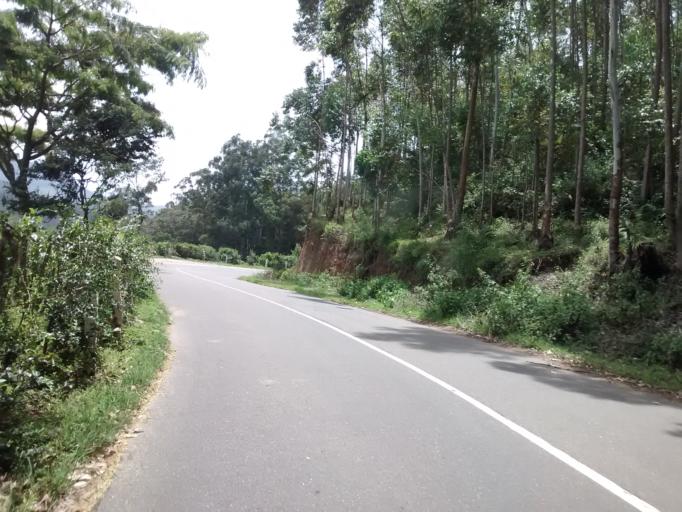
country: IN
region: Kerala
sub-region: Idukki
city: Munnar
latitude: 10.1332
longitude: 77.1730
